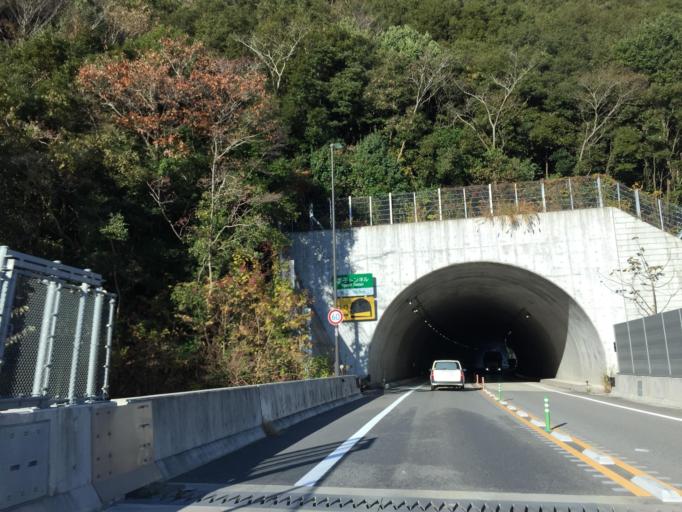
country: JP
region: Wakayama
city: Wakayama-shi
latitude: 34.2862
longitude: 135.1557
